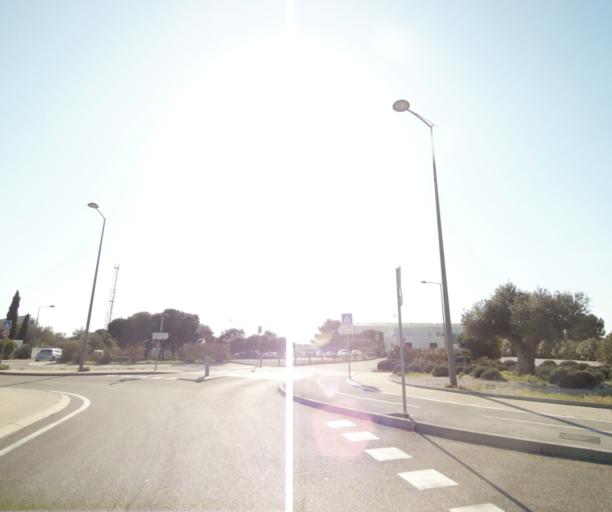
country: FR
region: Languedoc-Roussillon
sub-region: Departement de l'Herault
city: Jacou
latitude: 43.6455
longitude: 3.9178
